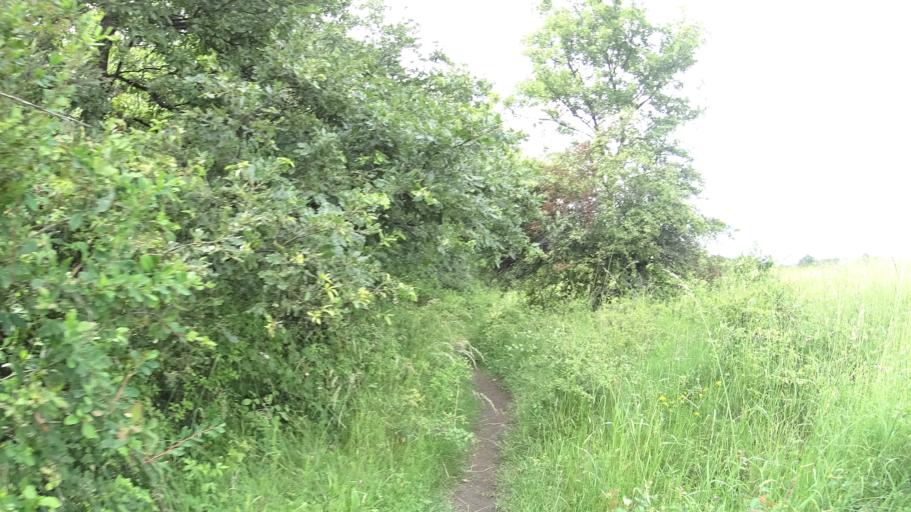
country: HU
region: Pest
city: Nagymaros
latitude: 47.8272
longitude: 18.9450
